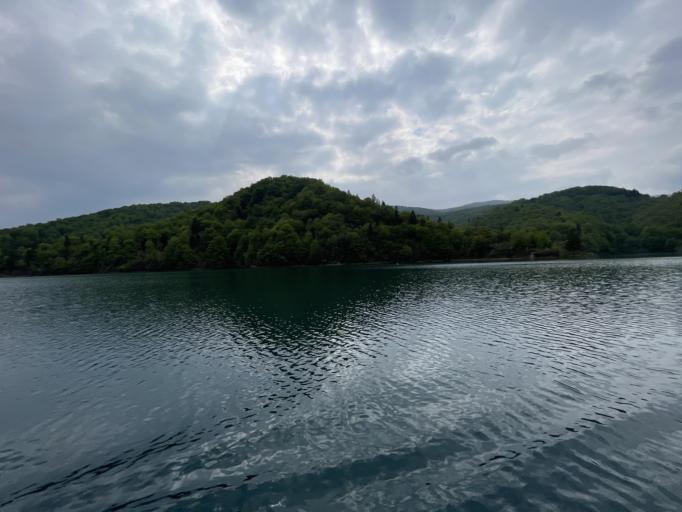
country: HR
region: Licko-Senjska
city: Jezerce
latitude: 44.8910
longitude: 15.6050
